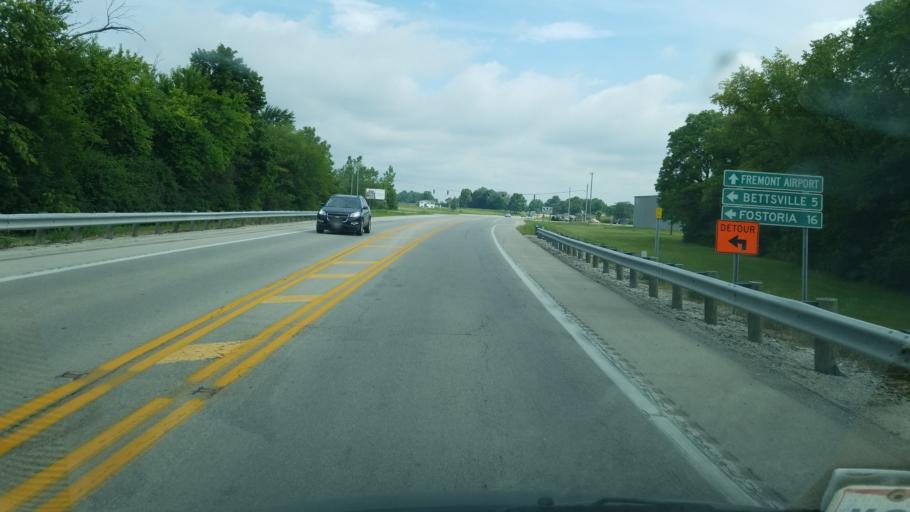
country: US
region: Ohio
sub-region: Sandusky County
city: Ballville
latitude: 41.2898
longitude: -83.1714
